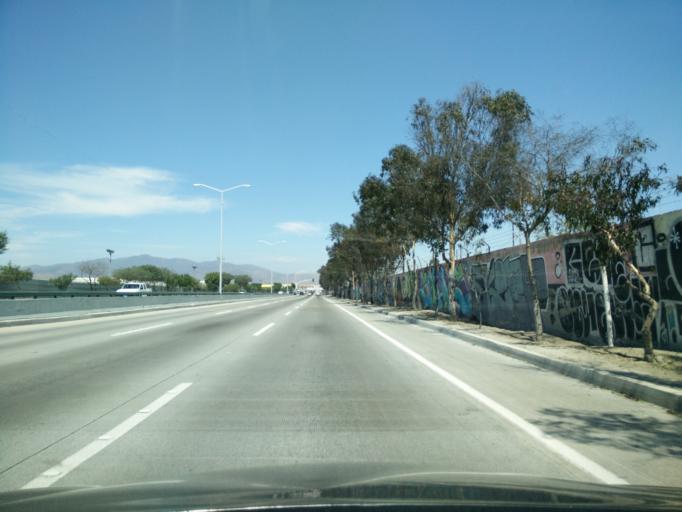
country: MX
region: Baja California
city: Tijuana
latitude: 32.5462
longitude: -116.9831
